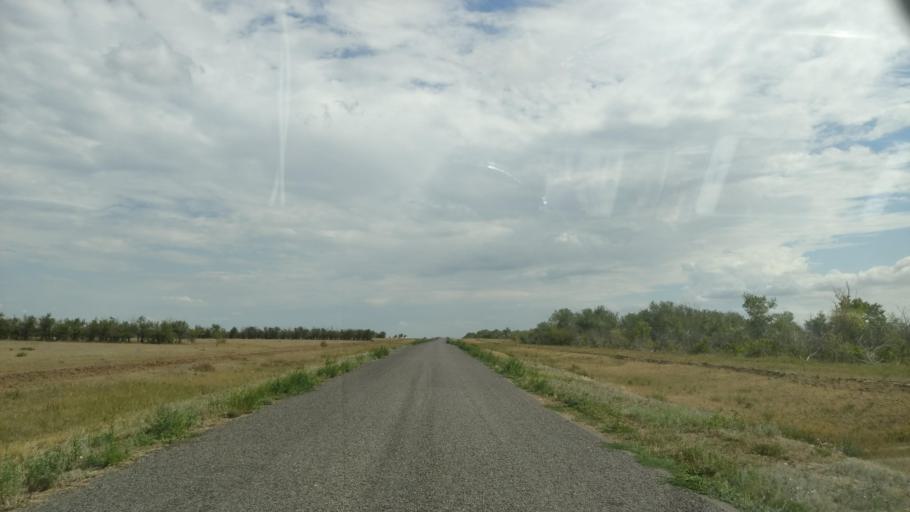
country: KZ
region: Pavlodar
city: Pavlodar
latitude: 52.6372
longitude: 76.9950
